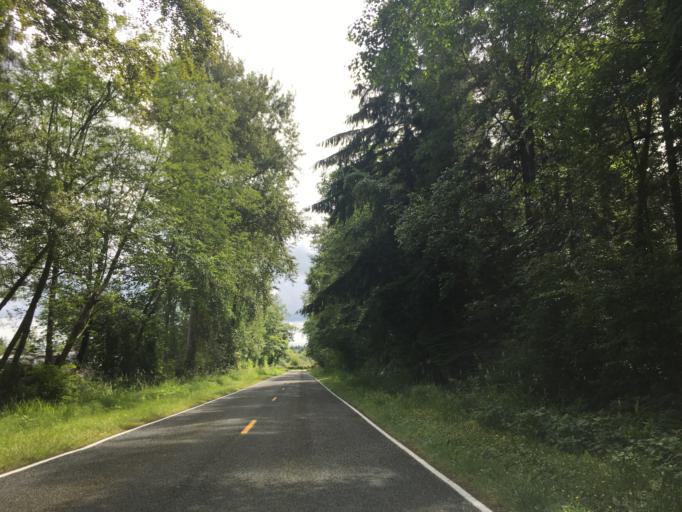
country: US
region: Washington
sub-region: Whatcom County
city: Birch Bay
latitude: 48.9033
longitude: -122.7527
